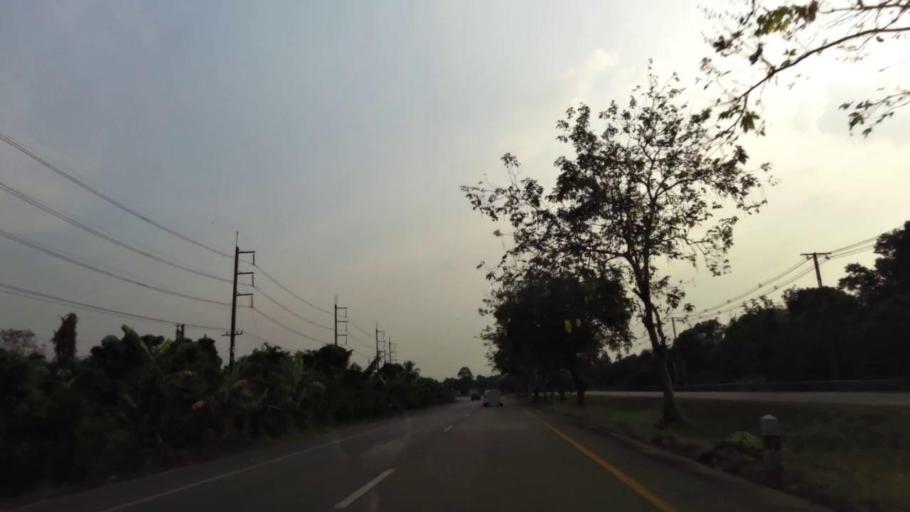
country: TH
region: Chanthaburi
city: Chanthaburi
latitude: 12.5319
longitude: 102.1574
